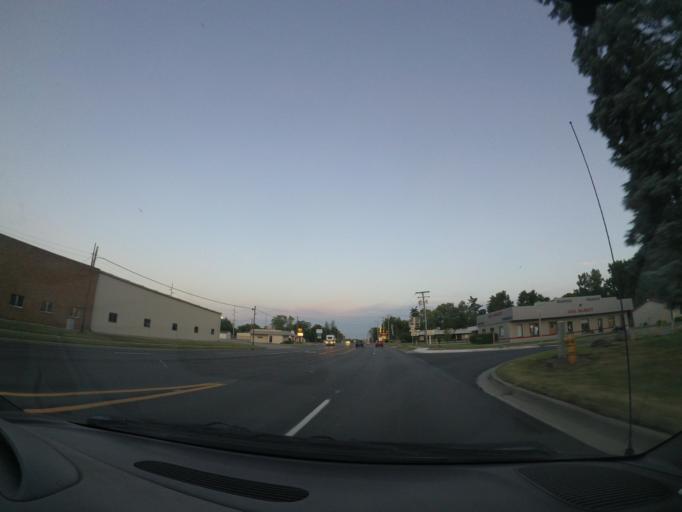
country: US
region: Indiana
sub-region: Elkhart County
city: Dunlap
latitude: 41.6495
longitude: -85.9390
